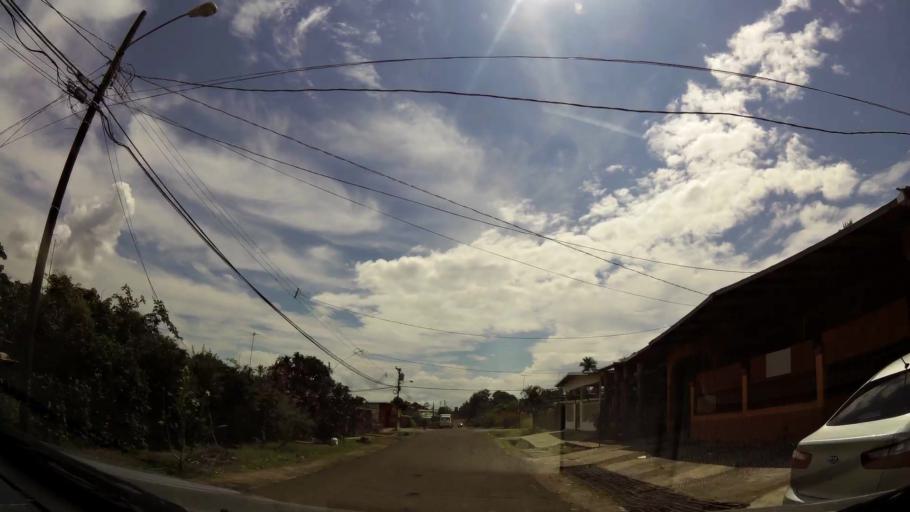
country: PA
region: Panama
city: Vista Alegre
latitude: 8.9286
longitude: -79.6993
